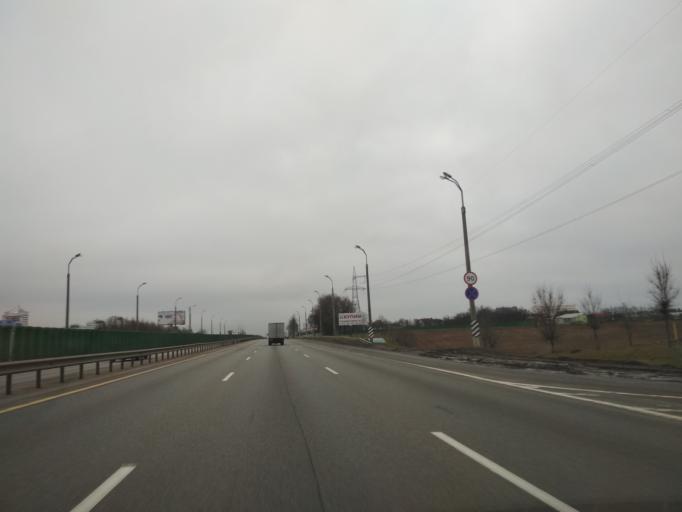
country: BY
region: Minsk
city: Shchomyslitsa
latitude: 53.8437
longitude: 27.4574
